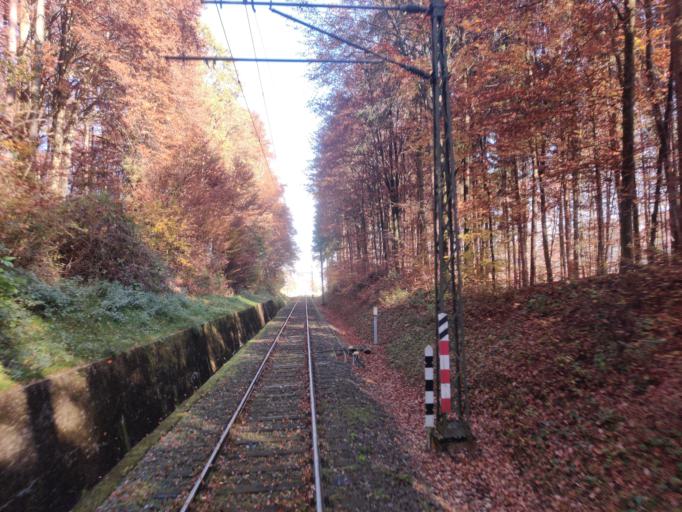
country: AT
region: Styria
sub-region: Politischer Bezirk Suedoststeiermark
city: Feldbach
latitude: 46.9396
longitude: 15.8778
